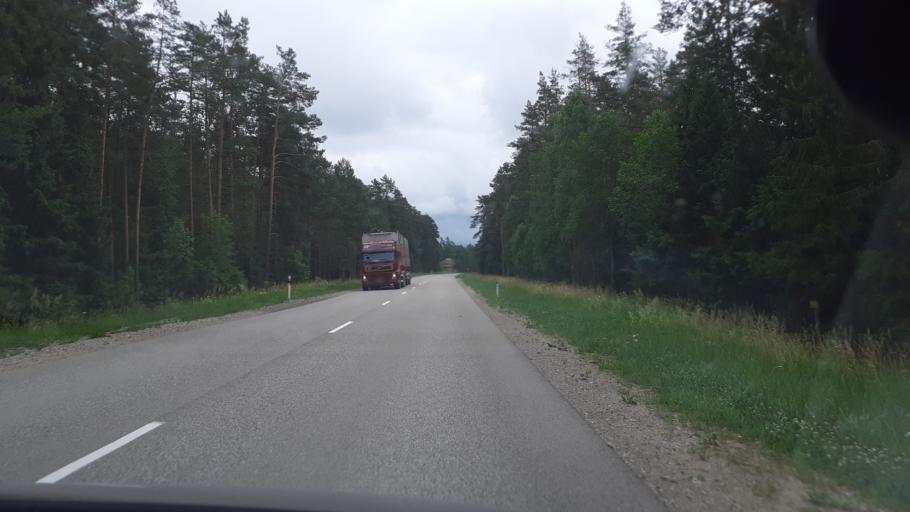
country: LV
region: Ventspils Rajons
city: Piltene
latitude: 57.1082
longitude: 21.7683
